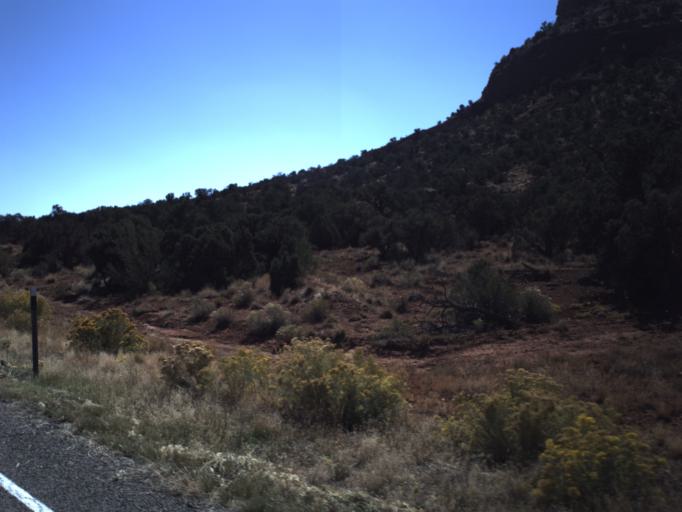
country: US
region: Utah
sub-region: San Juan County
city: Blanding
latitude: 37.6323
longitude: -110.0928
